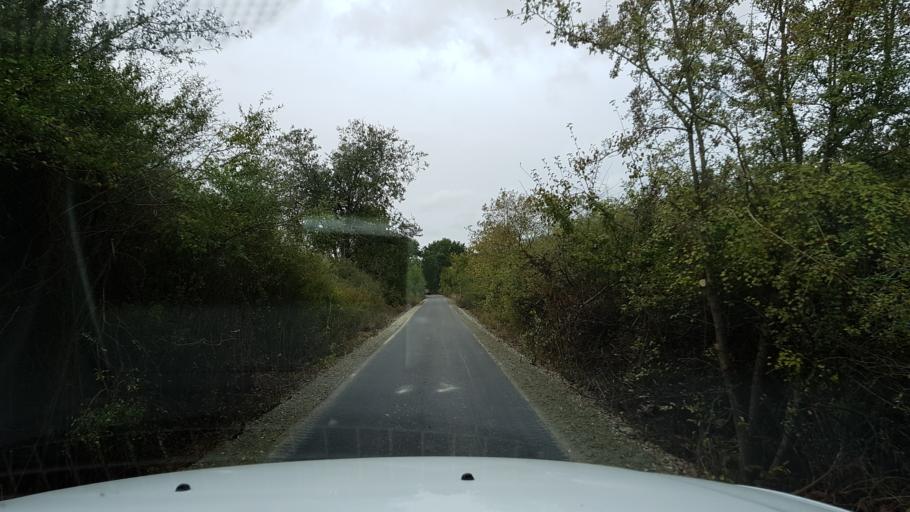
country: PL
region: West Pomeranian Voivodeship
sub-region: Powiat gryfinski
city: Moryn
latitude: 52.8745
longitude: 14.3849
